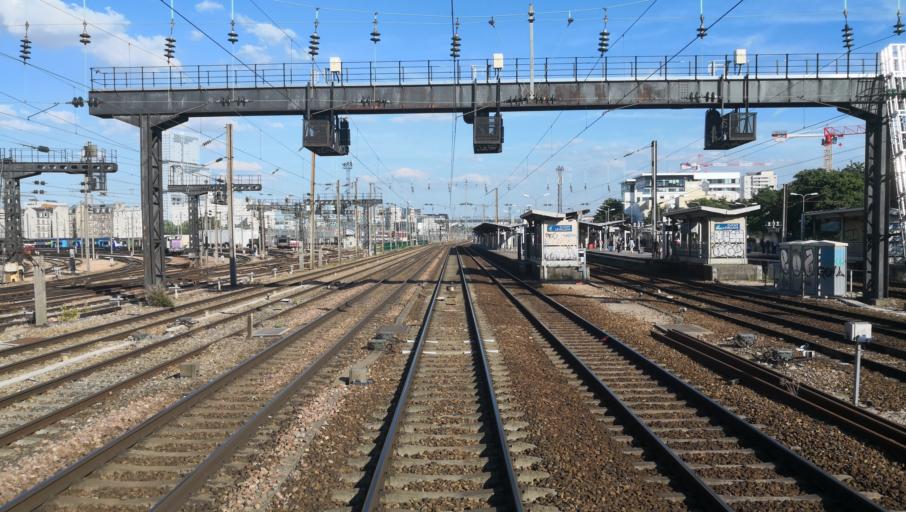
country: FR
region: Ile-de-France
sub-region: Departement des Hauts-de-Seine
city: Levallois-Perret
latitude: 48.8983
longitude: 2.2966
